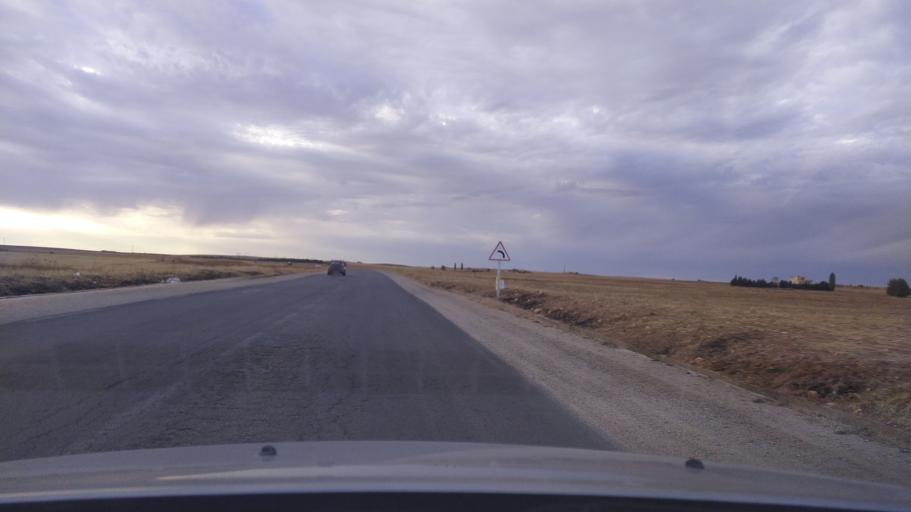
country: DZ
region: Tiaret
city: Frenda
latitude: 34.9791
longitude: 1.1519
